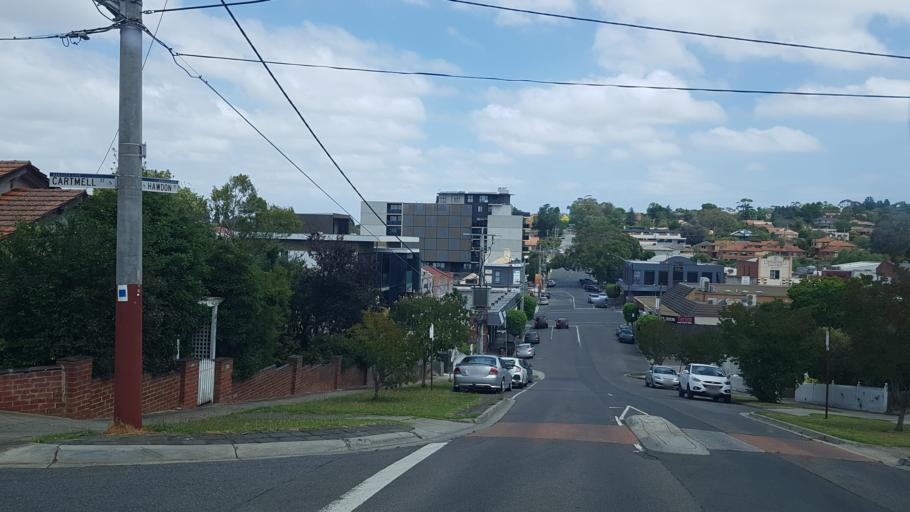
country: AU
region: Victoria
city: Rosanna
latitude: -37.7549
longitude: 145.0648
